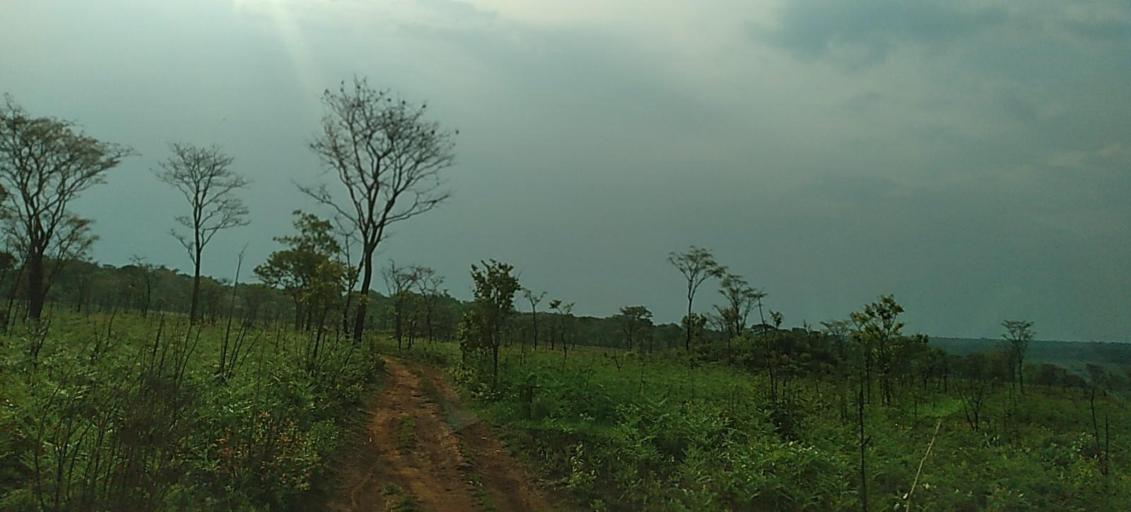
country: ZM
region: North-Western
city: Solwezi
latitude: -12.0420
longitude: 26.0445
